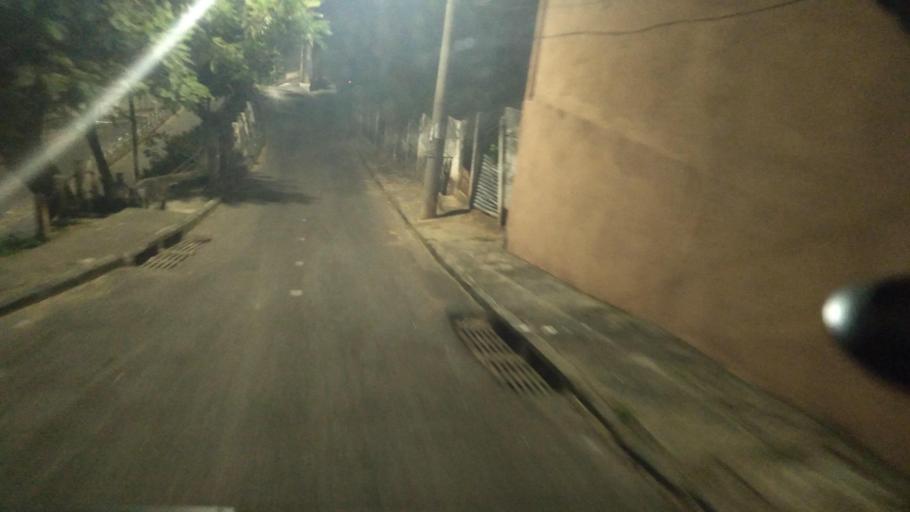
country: BR
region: Minas Gerais
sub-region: Belo Horizonte
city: Belo Horizonte
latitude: -19.8890
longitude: -43.9597
